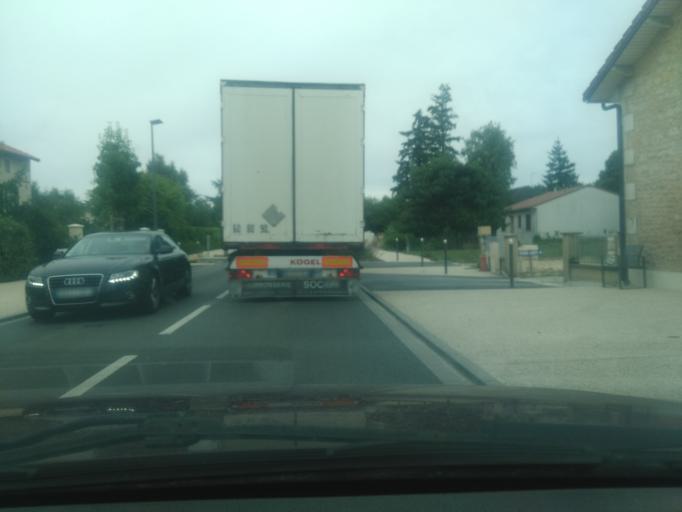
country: FR
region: Poitou-Charentes
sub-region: Departement de la Vienne
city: Savigny-Levescault
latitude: 46.5588
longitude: 0.5008
